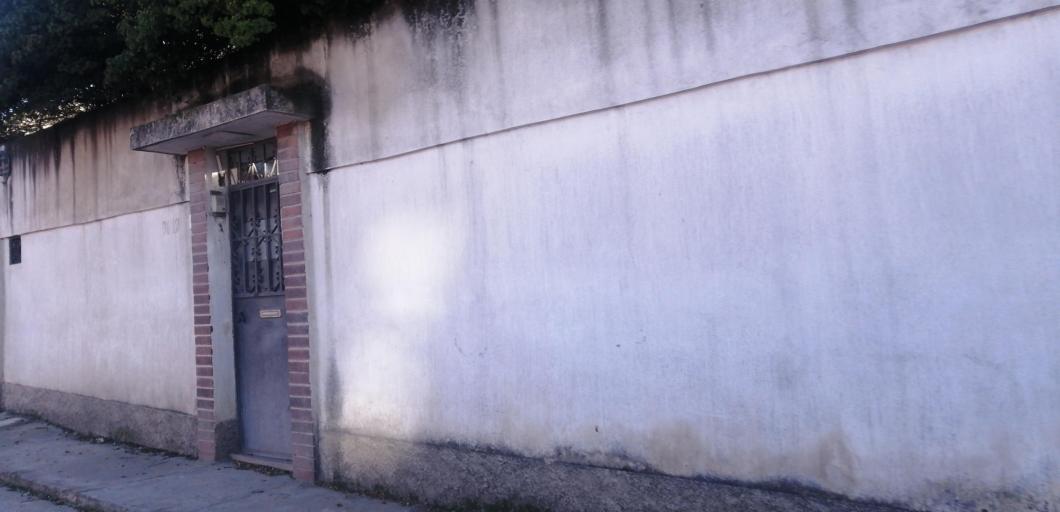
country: GT
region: Quetzaltenango
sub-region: Municipio de La Esperanza
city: La Esperanza
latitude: 14.8643
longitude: -91.5384
